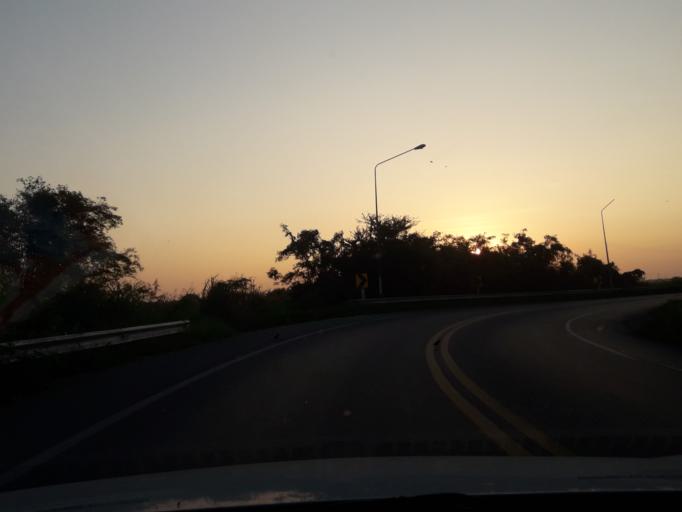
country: TH
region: Phra Nakhon Si Ayutthaya
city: Maha Rat
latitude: 14.5254
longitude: 100.5369
